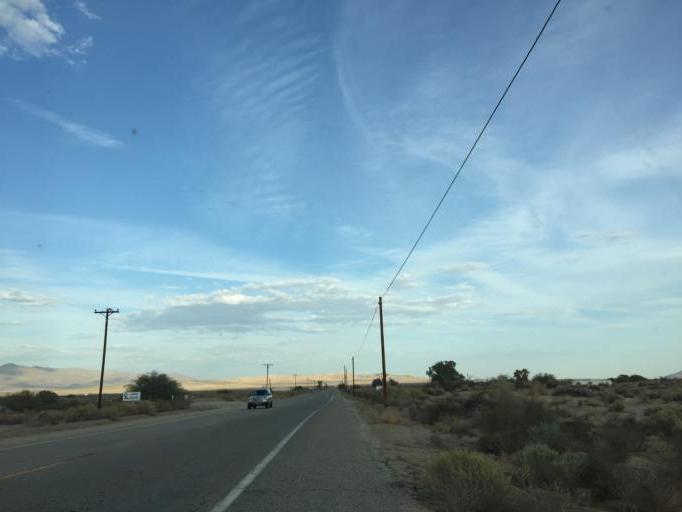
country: US
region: California
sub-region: San Diego County
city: Borrego Springs
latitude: 33.2569
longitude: -116.3371
